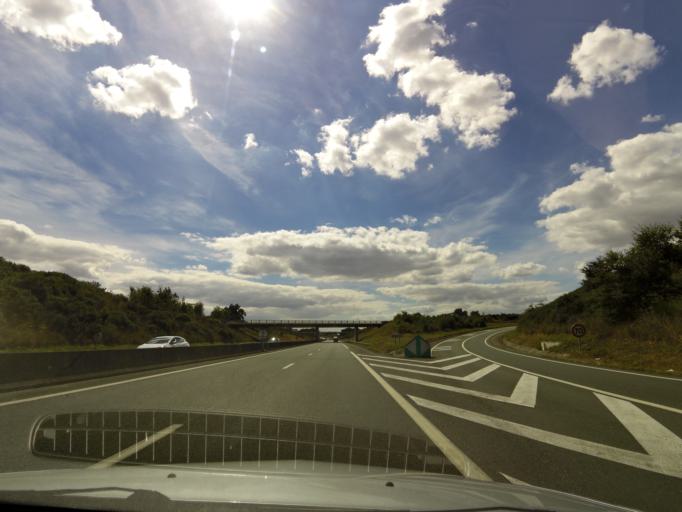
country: FR
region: Pays de la Loire
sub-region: Departement de la Vendee
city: La Ferriere
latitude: 46.6706
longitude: -1.3512
